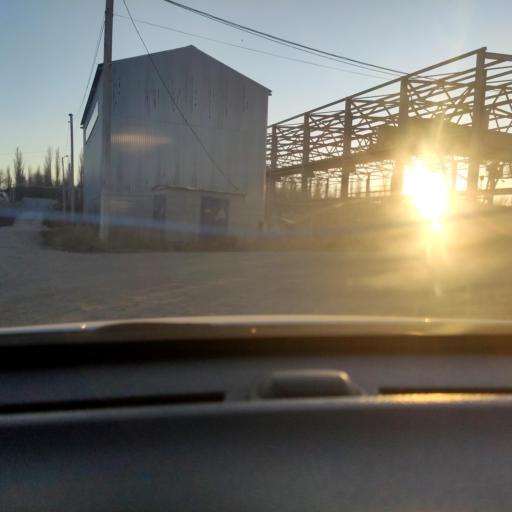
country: RU
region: Voronezj
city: Maslovka
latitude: 51.6112
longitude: 39.2424
